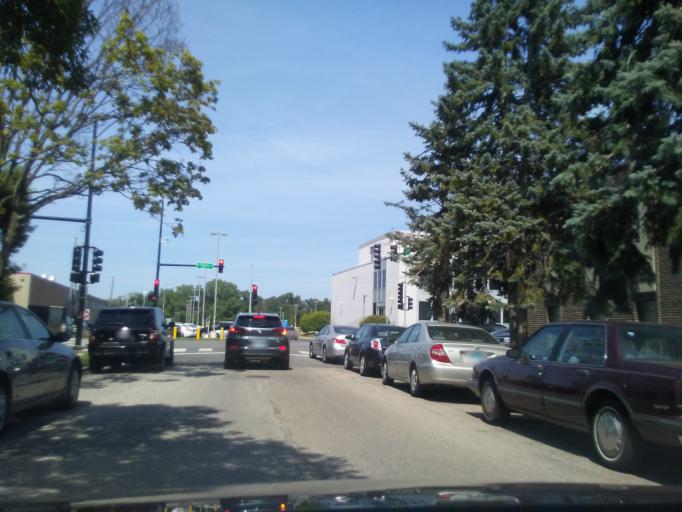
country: US
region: Illinois
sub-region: Cook County
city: Lincolnwood
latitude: 41.9796
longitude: -87.7597
